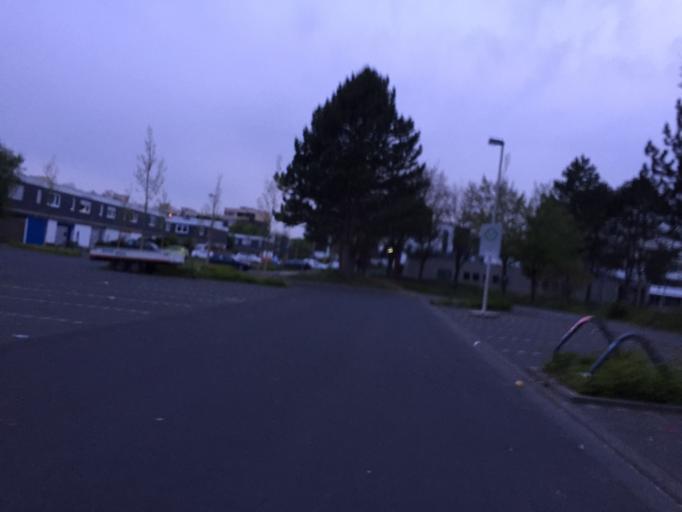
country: DE
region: North Rhine-Westphalia
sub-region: Regierungsbezirk Koln
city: Alfter
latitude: 50.7505
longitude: 7.0426
